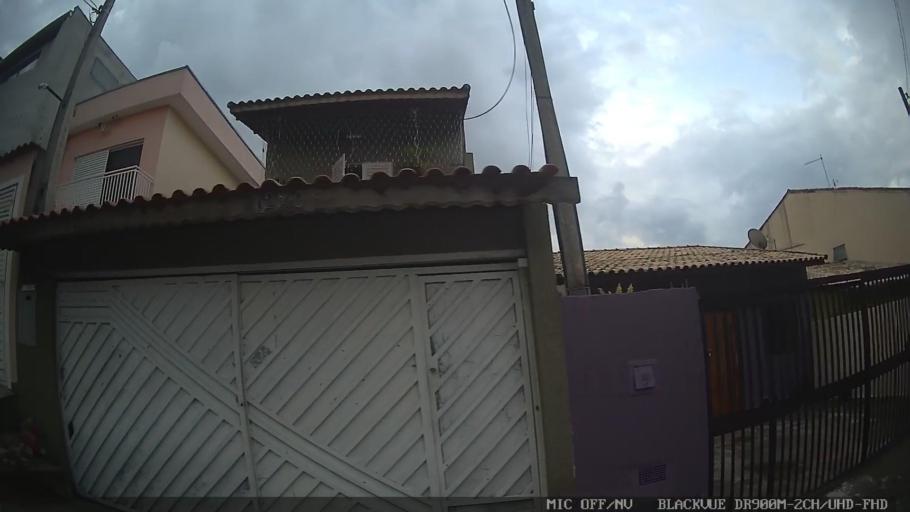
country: BR
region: Sao Paulo
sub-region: Mogi das Cruzes
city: Mogi das Cruzes
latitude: -23.5447
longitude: -46.1947
